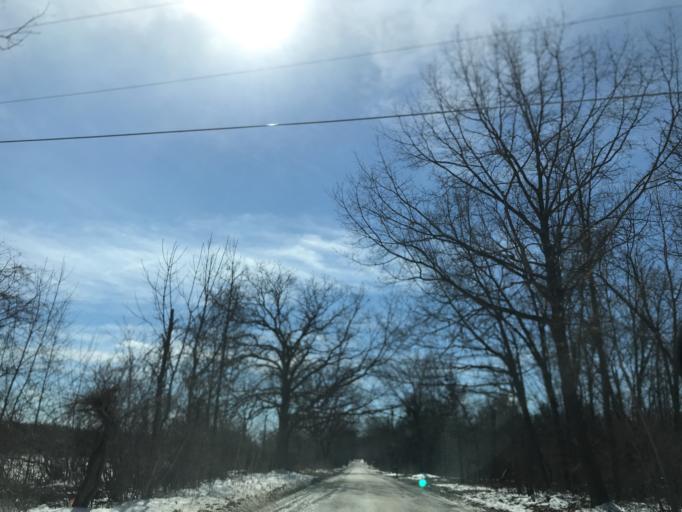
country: US
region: Michigan
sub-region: Livingston County
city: Whitmore Lake
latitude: 42.4171
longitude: -83.7243
